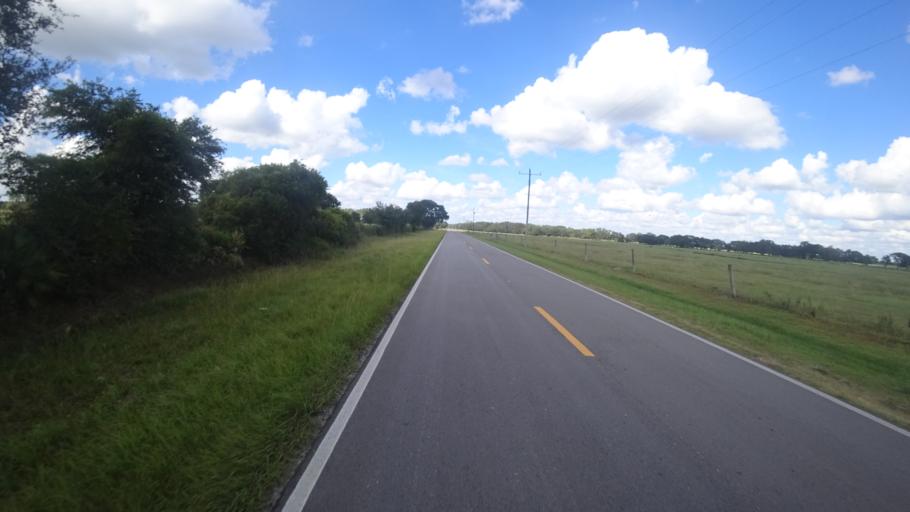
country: US
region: Florida
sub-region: Sarasota County
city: Warm Mineral Springs
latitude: 27.2798
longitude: -82.2119
